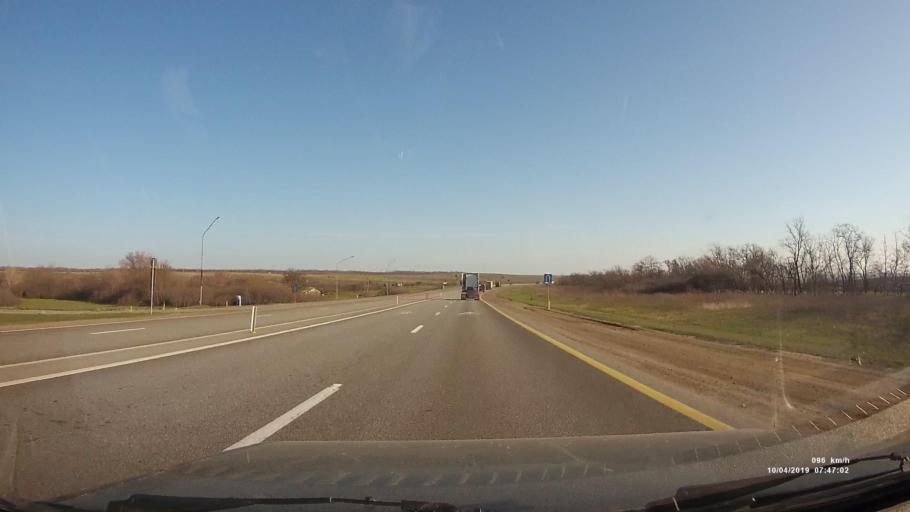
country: RU
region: Rostov
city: Kamensk-Shakhtinskiy
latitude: 48.2157
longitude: 40.2701
